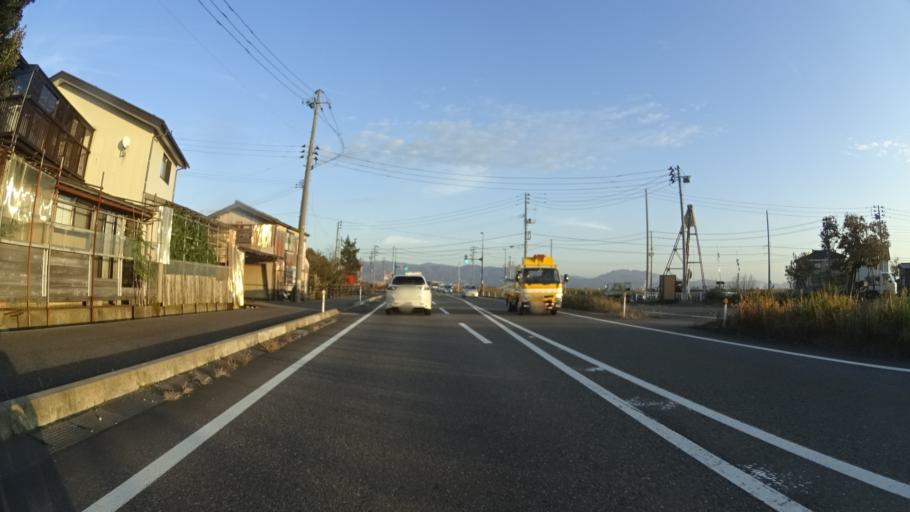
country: JP
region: Niigata
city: Nagaoka
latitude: 37.4364
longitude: 138.8034
